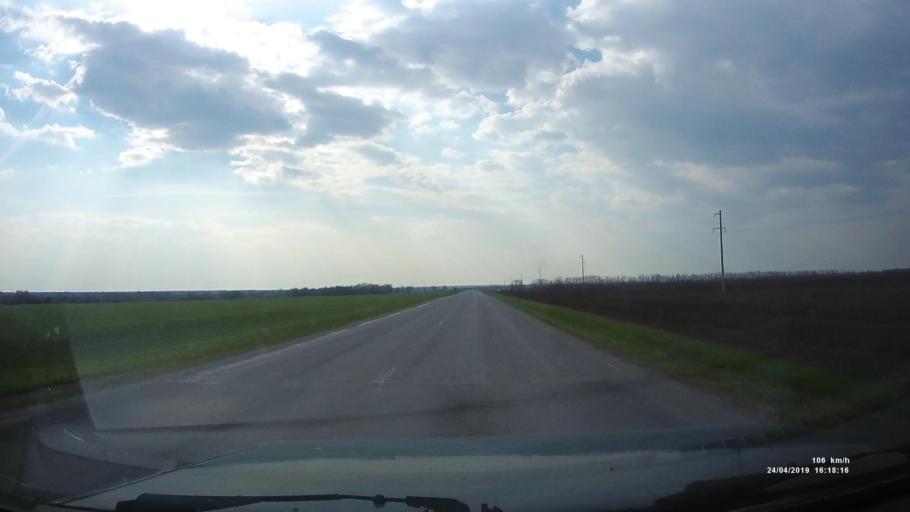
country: RU
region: Rostov
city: Sovetskoye
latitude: 46.7735
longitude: 42.1199
